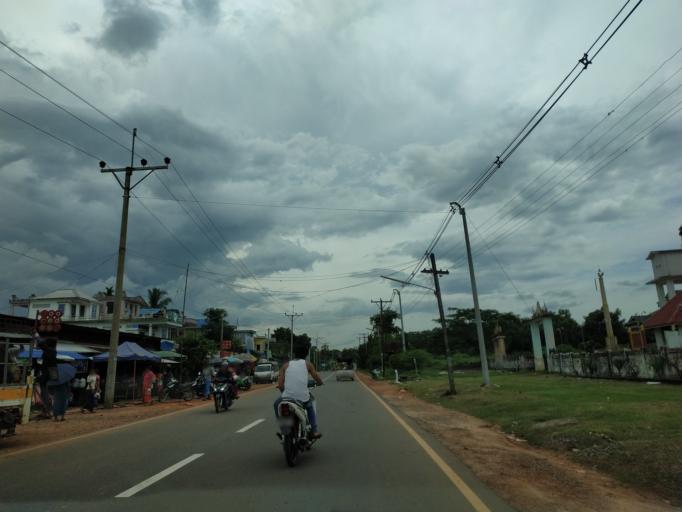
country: MM
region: Tanintharyi
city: Dawei
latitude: 14.0112
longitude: 98.2266
